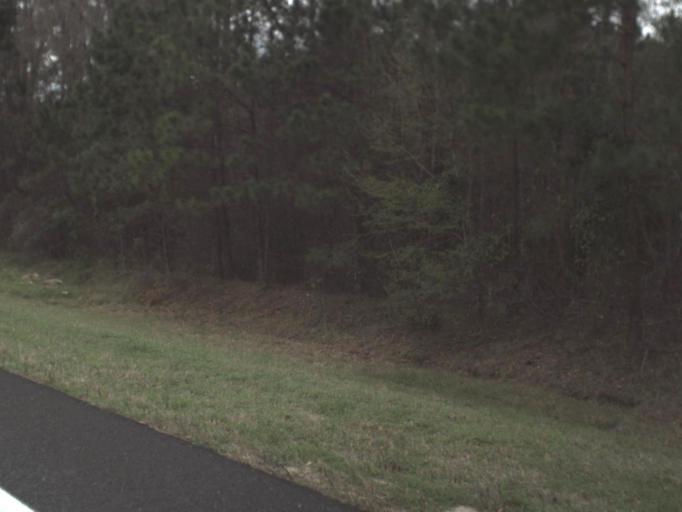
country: US
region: Georgia
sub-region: Grady County
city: Cairo
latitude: 30.6518
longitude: -84.1691
